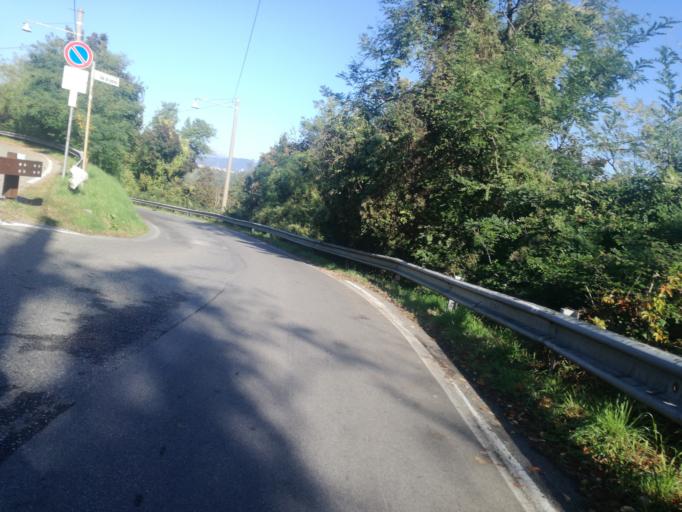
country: IT
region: Lombardy
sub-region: Citta metropolitana di Milano
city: Trezzo sull'Adda
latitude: 45.6144
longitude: 9.5151
